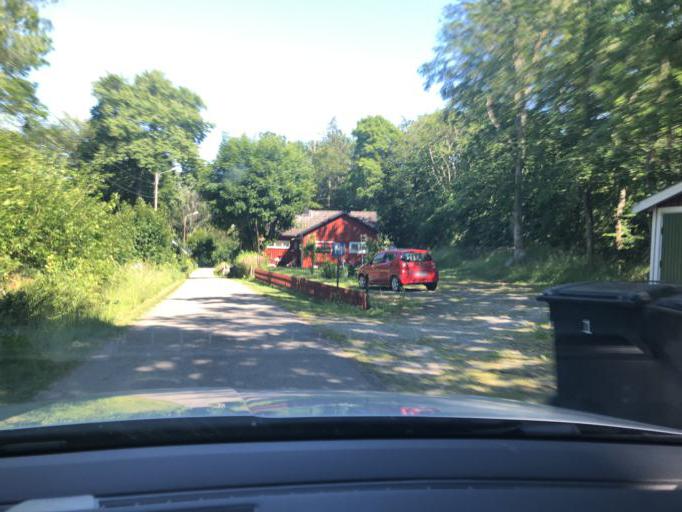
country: SE
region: Blekinge
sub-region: Karlshamns Kommun
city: Morrum
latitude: 56.1902
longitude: 14.6864
